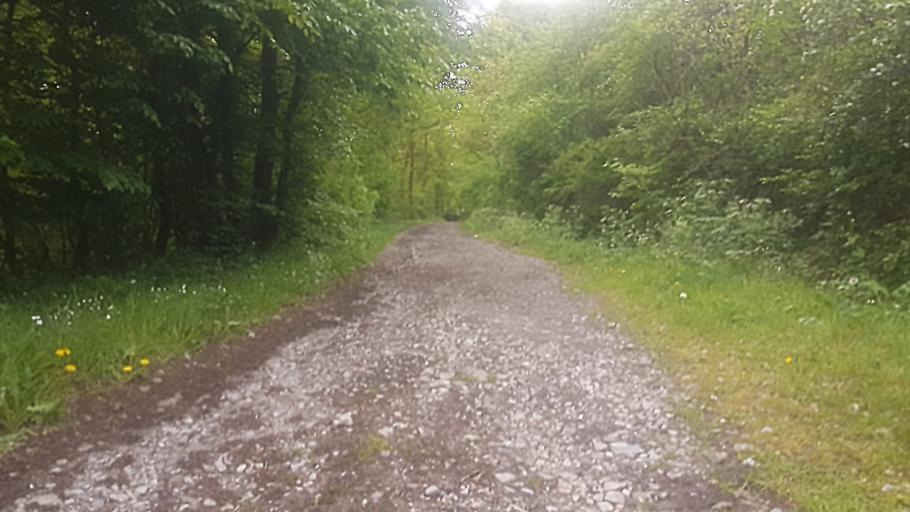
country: BE
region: Wallonia
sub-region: Province de Namur
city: Couvin
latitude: 50.0635
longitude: 4.6045
